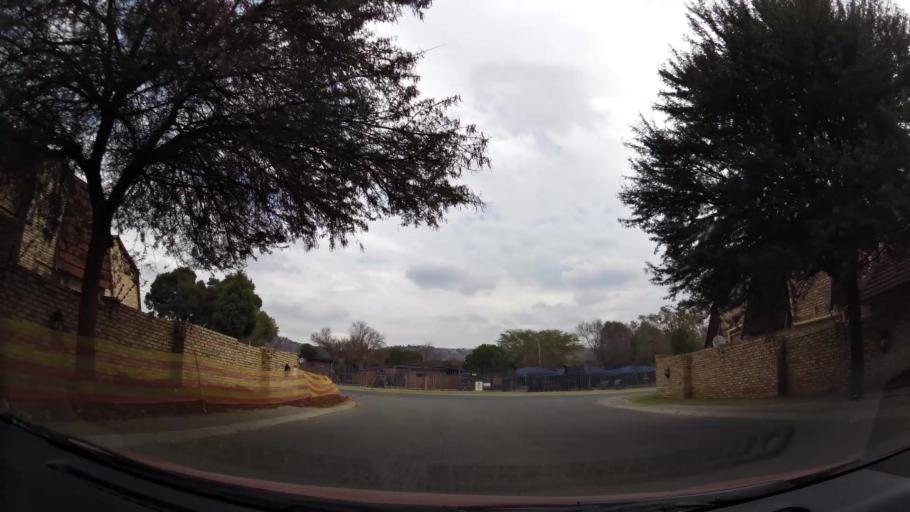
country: ZA
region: Gauteng
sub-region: West Rand District Municipality
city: Muldersdriseloop
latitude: -26.0928
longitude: 27.8772
